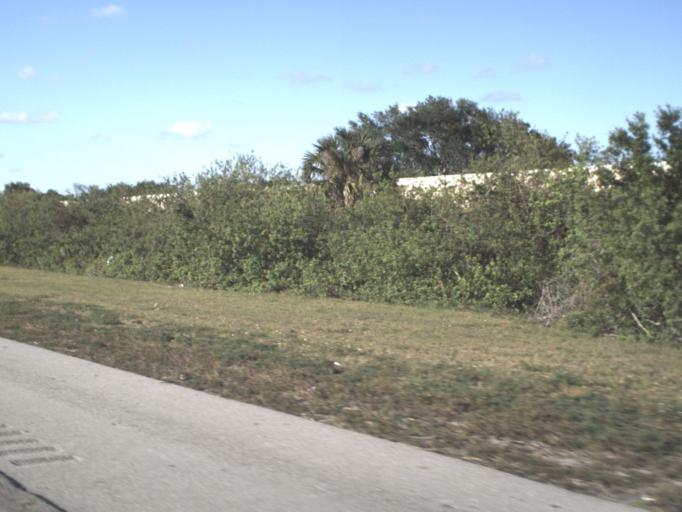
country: US
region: Florida
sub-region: Brevard County
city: Rockledge
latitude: 28.2514
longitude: -80.7245
